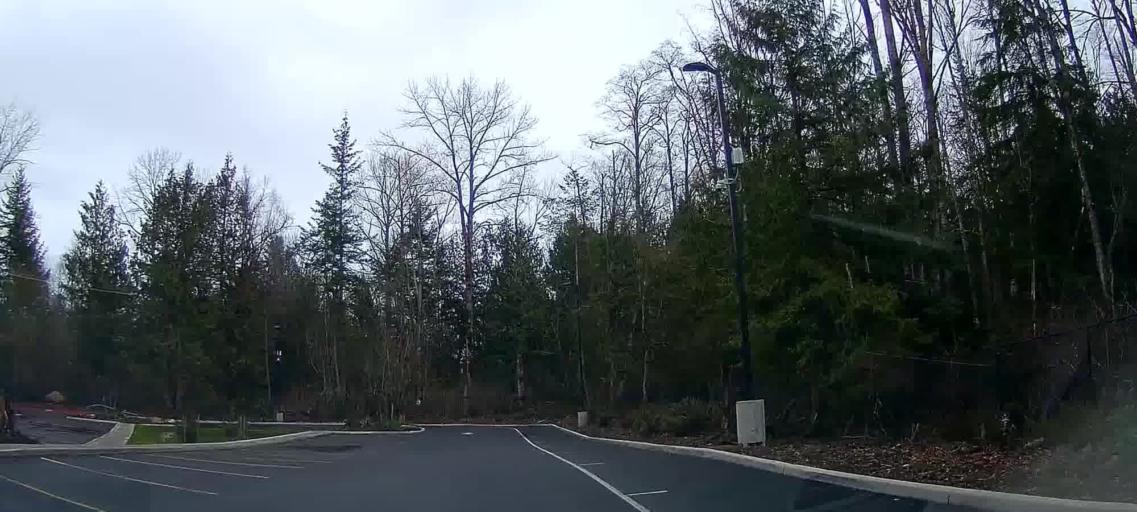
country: US
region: Washington
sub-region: Skagit County
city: Big Lake
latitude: 48.4228
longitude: -122.2721
